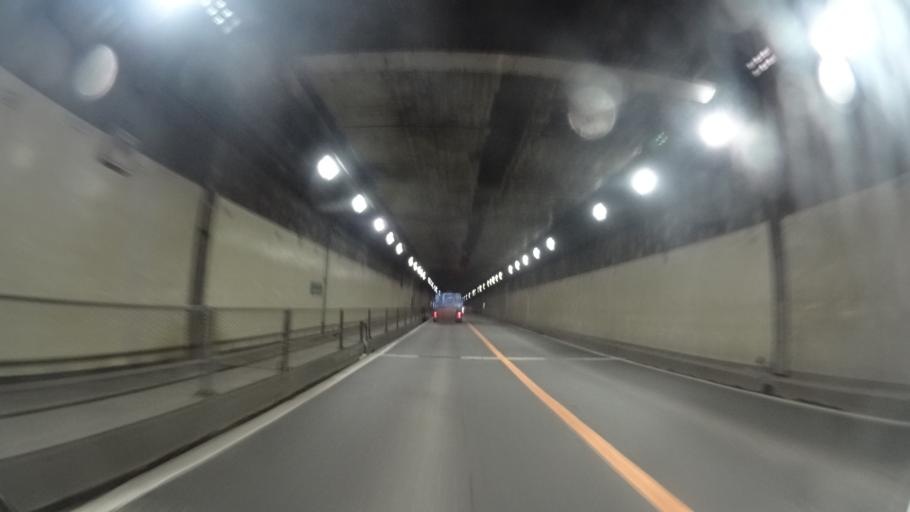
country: JP
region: Kumamoto
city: Ozu
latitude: 32.8351
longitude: 130.8551
